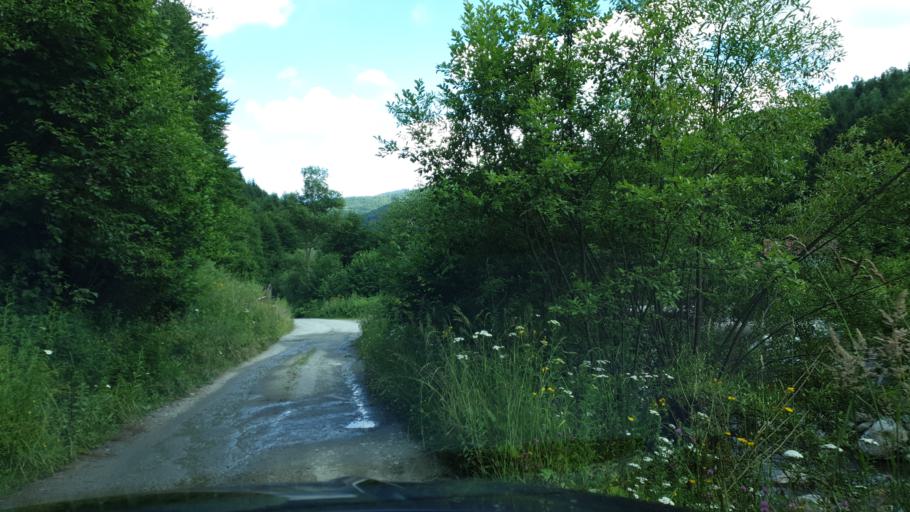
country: RO
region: Hunedoara
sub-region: Comuna Uricani
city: Uricani
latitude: 45.3019
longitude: 22.9901
